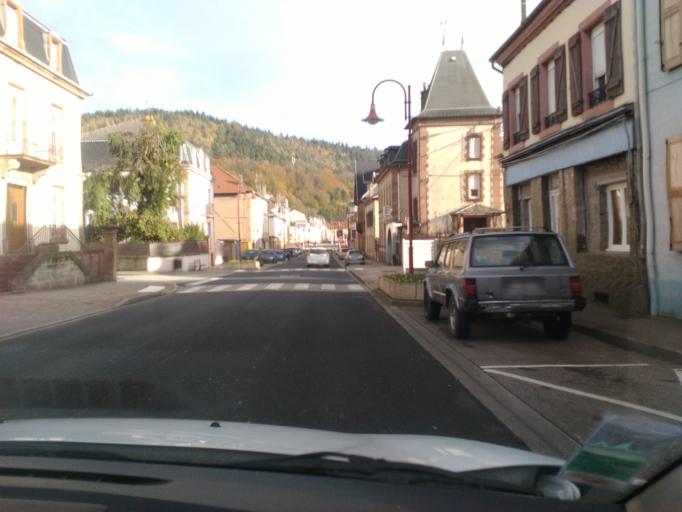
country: FR
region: Lorraine
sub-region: Departement des Vosges
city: Etival-Clairefontaine
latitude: 48.4047
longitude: 6.8403
